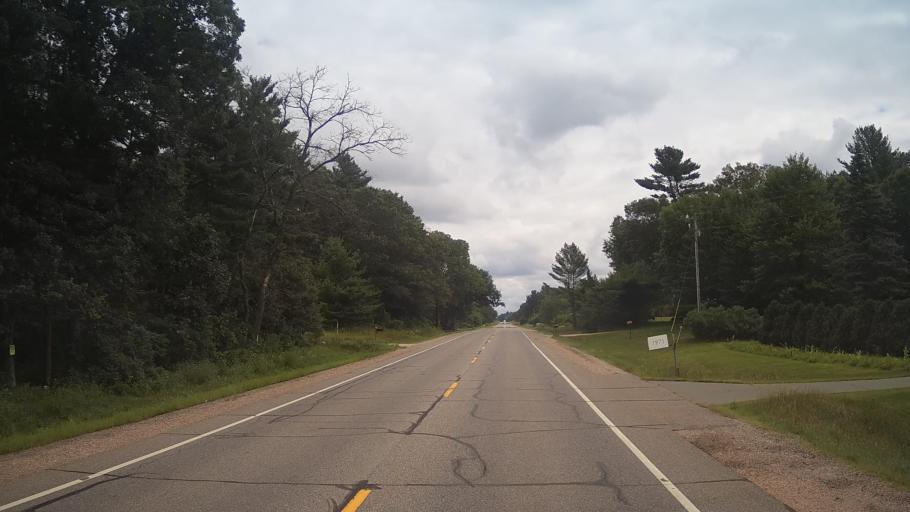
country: US
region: Wisconsin
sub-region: Adams County
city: Friendship
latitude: 44.0396
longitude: -89.9515
